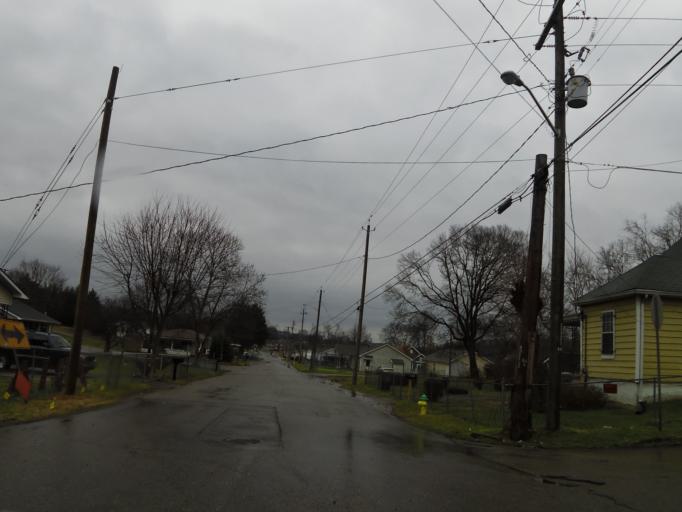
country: US
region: Tennessee
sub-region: Knox County
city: Knoxville
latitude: 35.9821
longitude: -83.9648
